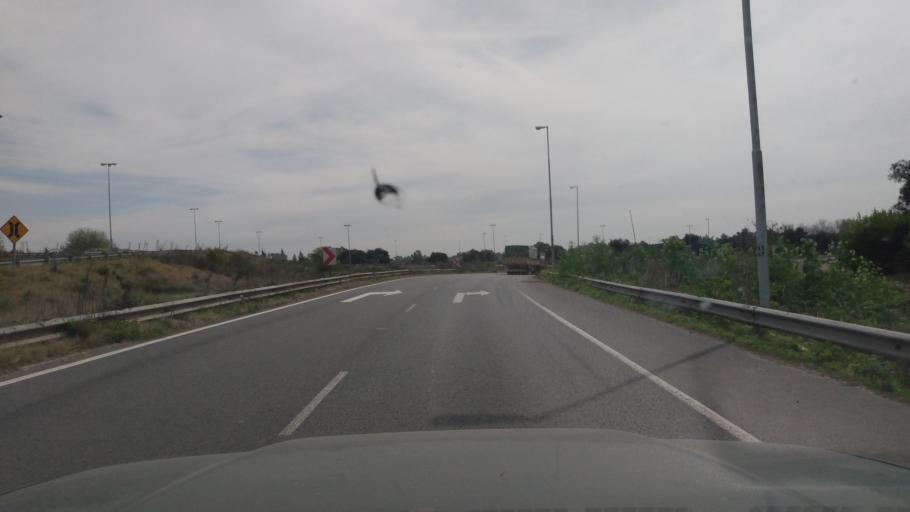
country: AR
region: Buenos Aires
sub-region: Partido de Lujan
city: Lujan
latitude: -34.4720
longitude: -59.0675
